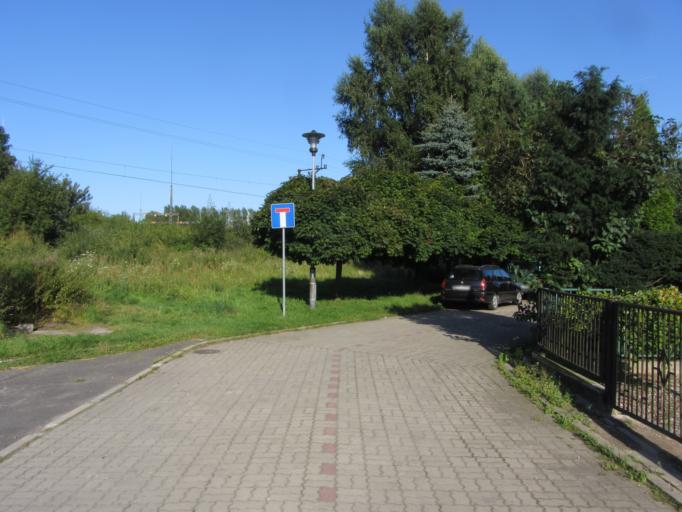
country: PL
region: West Pomeranian Voivodeship
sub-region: Powiat kolobrzeski
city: Kolobrzeg
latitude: 54.1750
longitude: 15.6008
